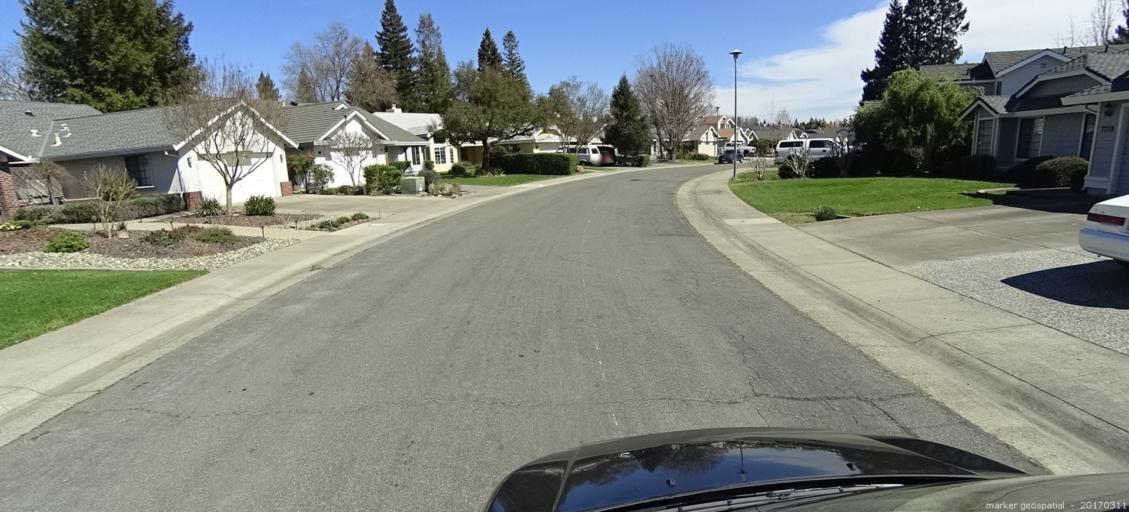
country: US
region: California
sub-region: Sacramento County
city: Parkway
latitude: 38.4833
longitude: -121.5419
